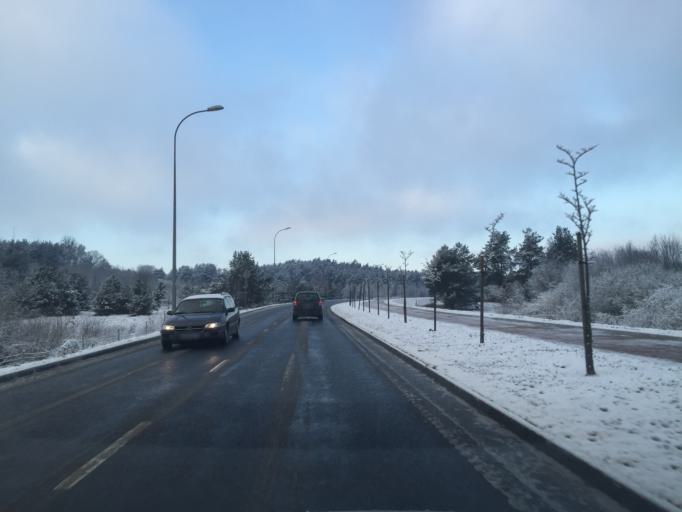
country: PL
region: Kujawsko-Pomorskie
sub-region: Powiat brodnicki
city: Brodnica
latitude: 53.2457
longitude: 19.3742
